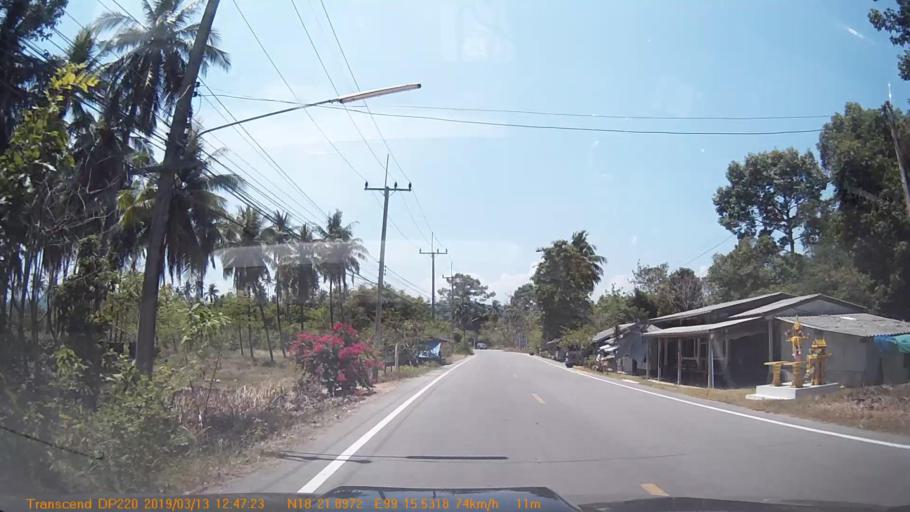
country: TH
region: Chumphon
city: Chumphon
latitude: 10.3649
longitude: 99.2584
